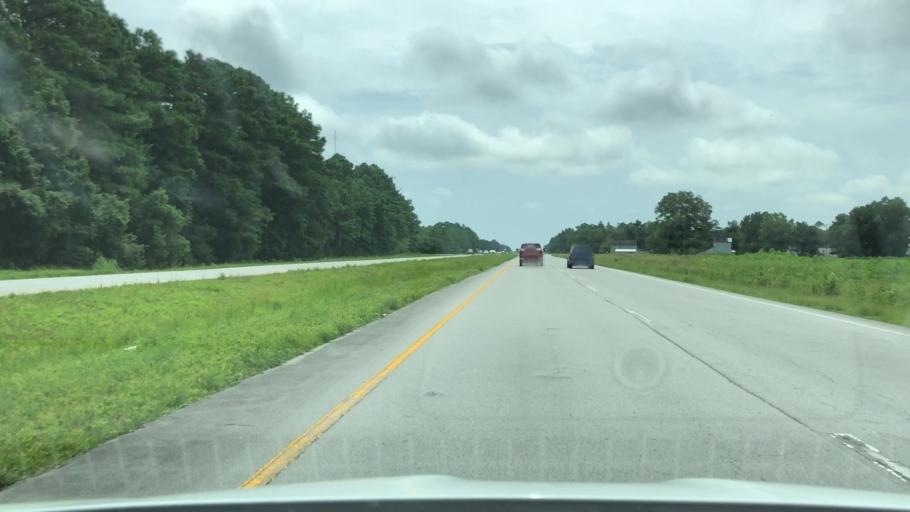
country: US
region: North Carolina
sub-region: Carteret County
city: Newport
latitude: 34.8087
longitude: -76.8795
